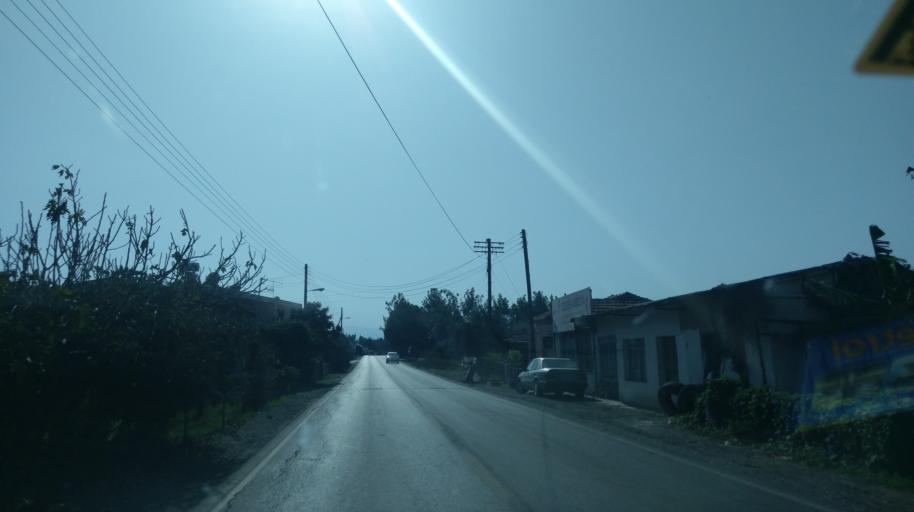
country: CY
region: Lefkosia
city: Morfou
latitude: 35.2100
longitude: 33.0013
